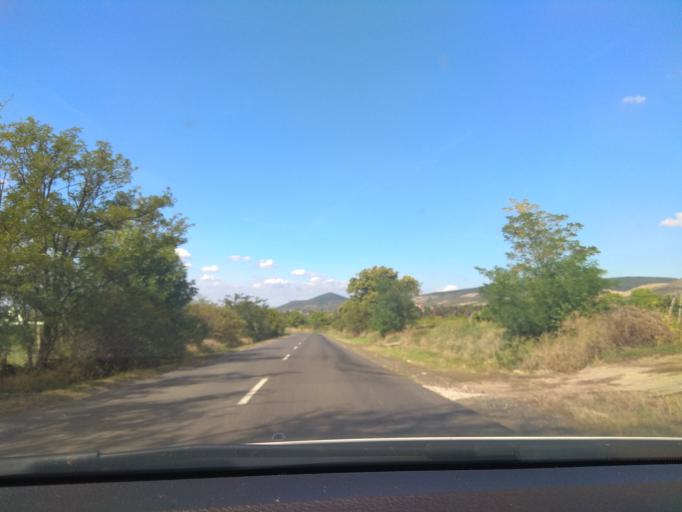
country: HU
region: Borsod-Abauj-Zemplen
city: Tallya
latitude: 48.2117
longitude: 21.2460
